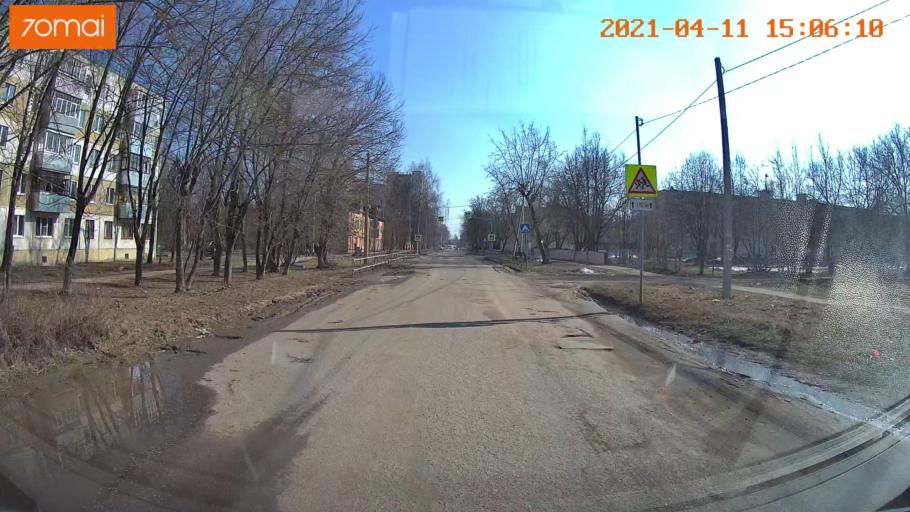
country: RU
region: Ivanovo
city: Bogorodskoye
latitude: 57.0199
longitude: 41.0160
